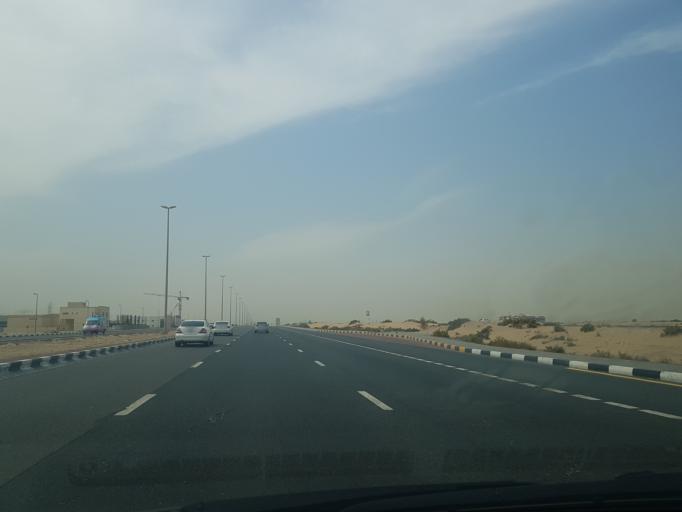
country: AE
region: Ash Shariqah
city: Sharjah
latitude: 25.2554
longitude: 55.5215
